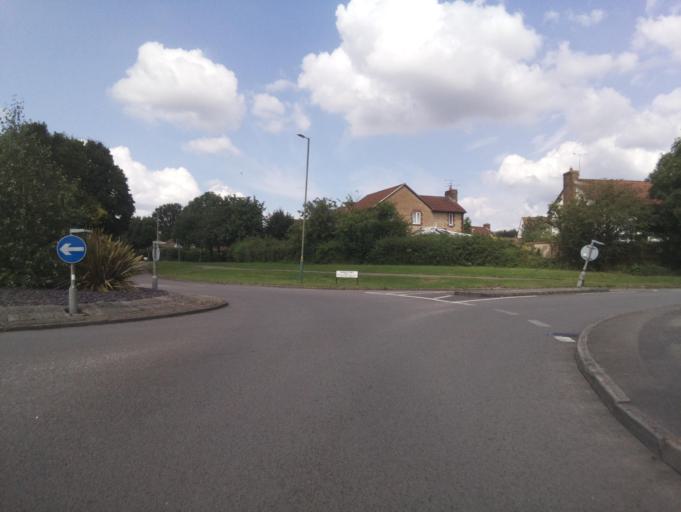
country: GB
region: England
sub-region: Wiltshire
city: Lydiard Tregoze
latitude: 51.5568
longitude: -1.8394
